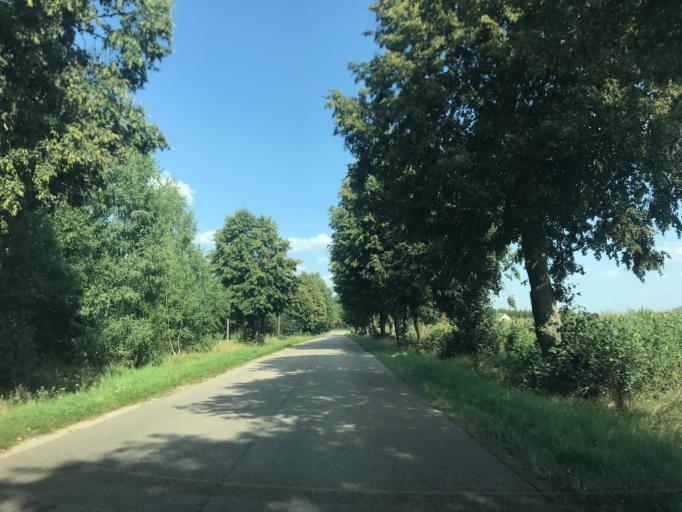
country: PL
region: Warmian-Masurian Voivodeship
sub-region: Powiat dzialdowski
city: Ilowo -Osada
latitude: 53.1099
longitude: 20.2976
